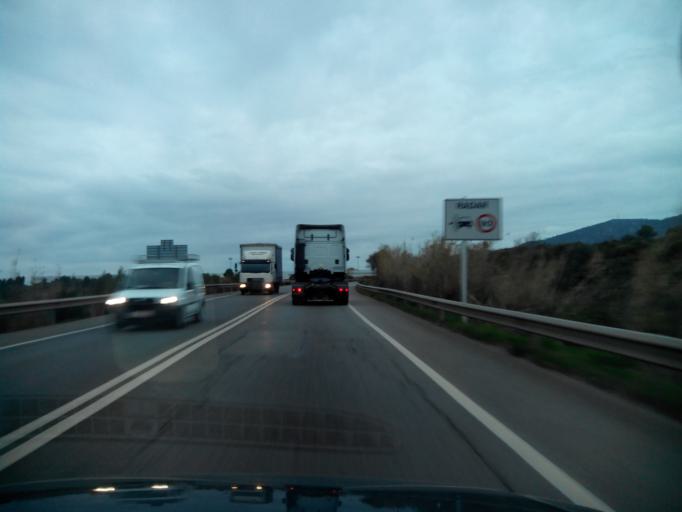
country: ES
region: Catalonia
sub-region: Provincia de Barcelona
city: Viladecavalls
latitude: 41.5602
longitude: 1.9727
